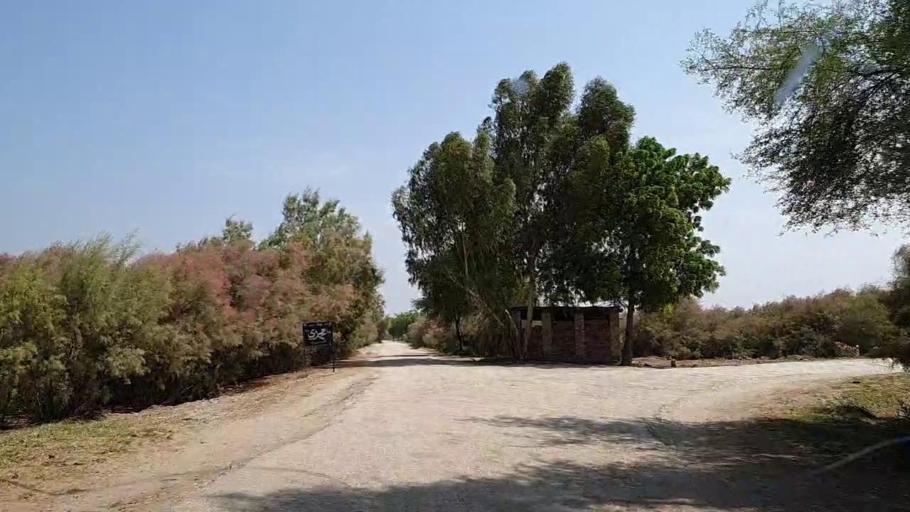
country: PK
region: Sindh
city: Khanpur
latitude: 27.8199
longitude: 69.3045
